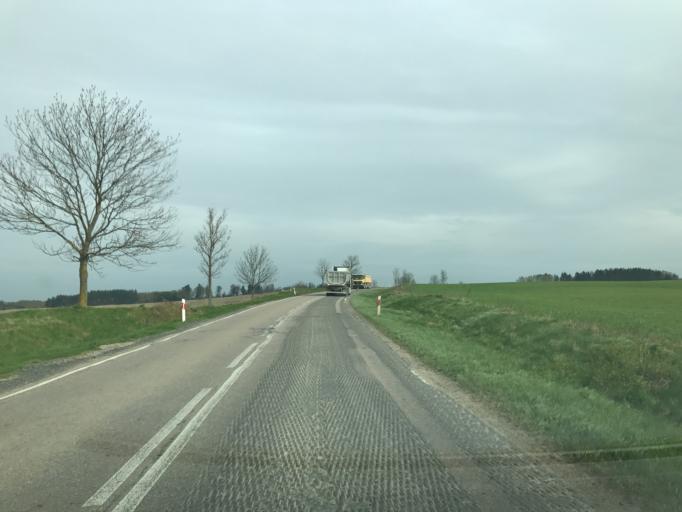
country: PL
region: Warmian-Masurian Voivodeship
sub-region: Powiat ostrodzki
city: Gierzwald
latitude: 53.5752
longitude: 20.0917
